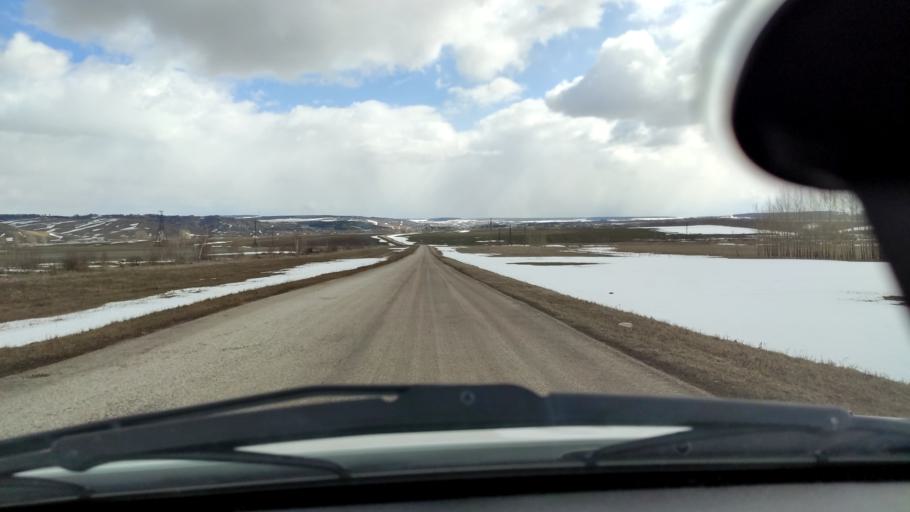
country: RU
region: Bashkortostan
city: Tolbazy
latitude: 54.1707
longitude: 55.9082
